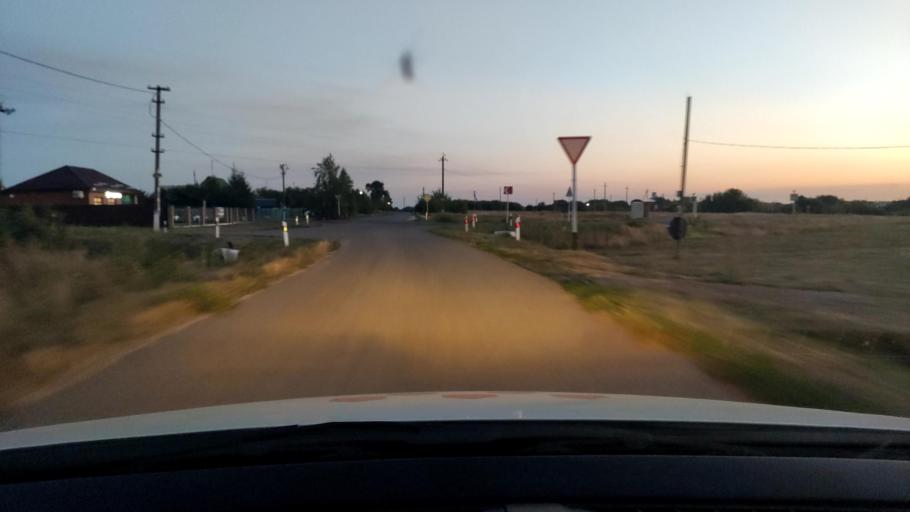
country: RU
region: Voronezj
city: Panino
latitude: 51.6514
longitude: 40.0193
